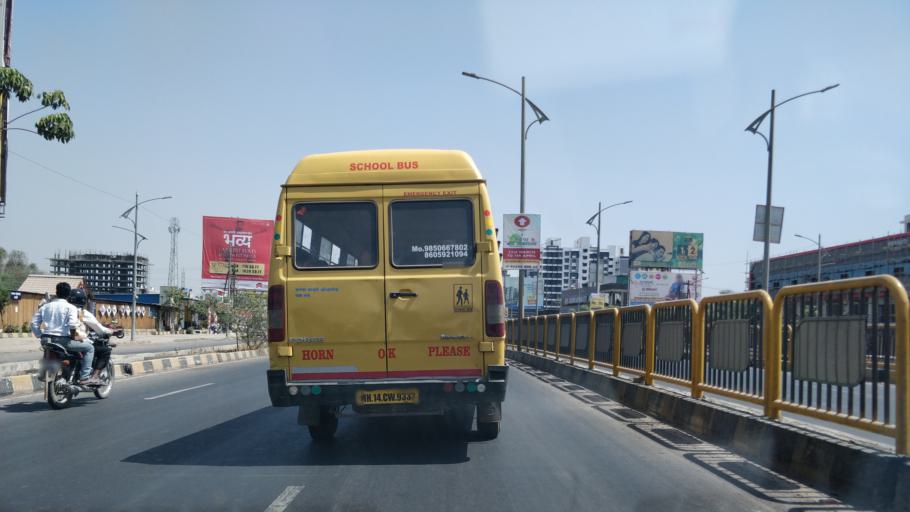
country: IN
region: Maharashtra
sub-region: Pune Division
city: Alandi
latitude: 18.6594
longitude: 73.8862
